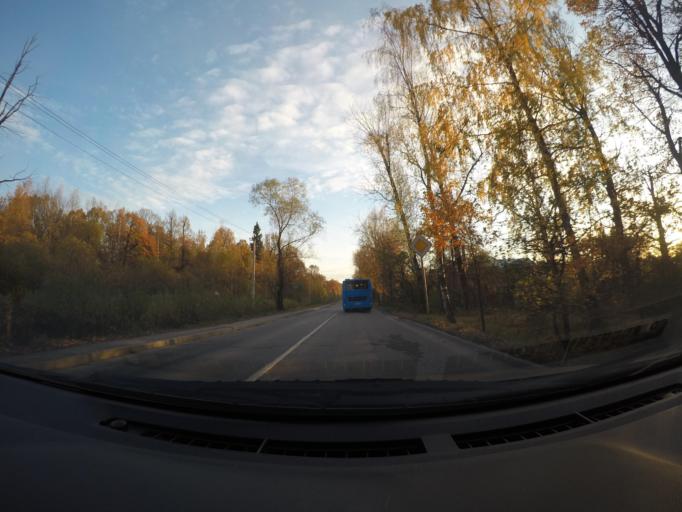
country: RU
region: Moskovskaya
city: Firsanovka
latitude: 55.9463
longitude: 37.2508
